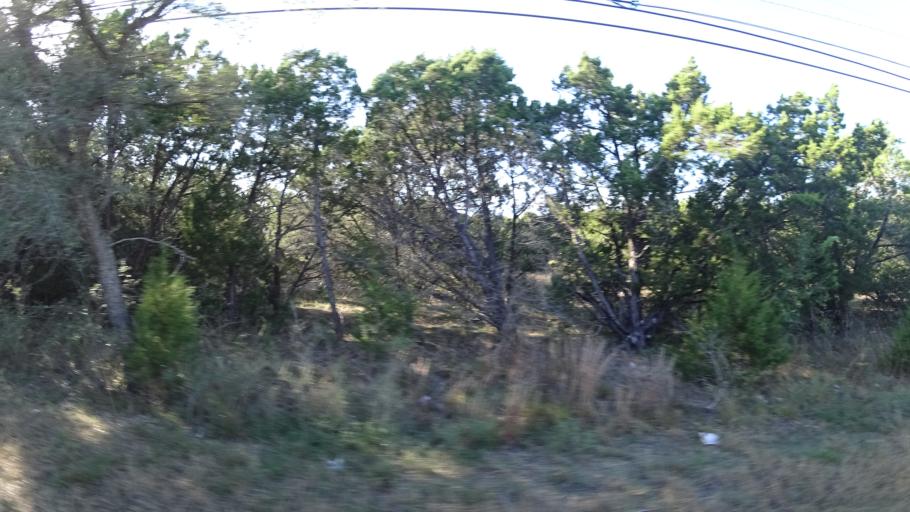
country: US
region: Texas
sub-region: Travis County
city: Barton Creek
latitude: 30.2510
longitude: -97.8478
